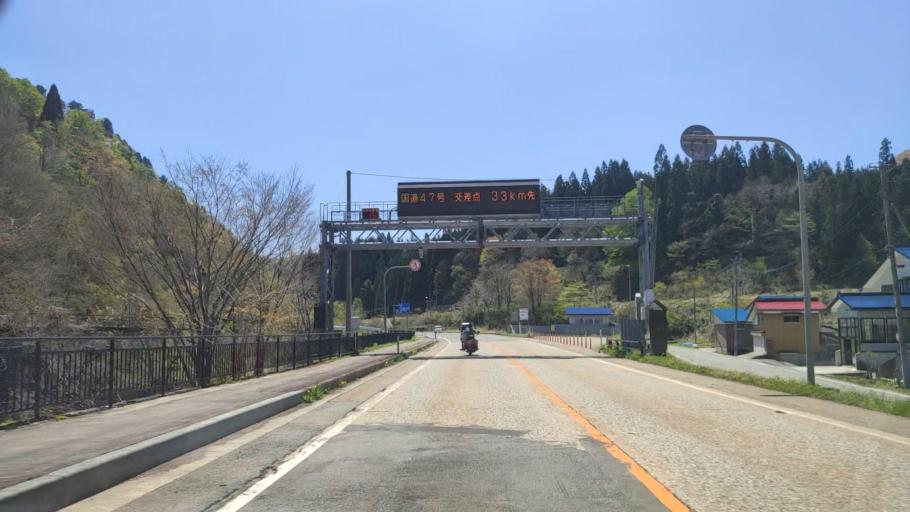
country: JP
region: Akita
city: Yuzawa
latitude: 38.9898
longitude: 140.3629
